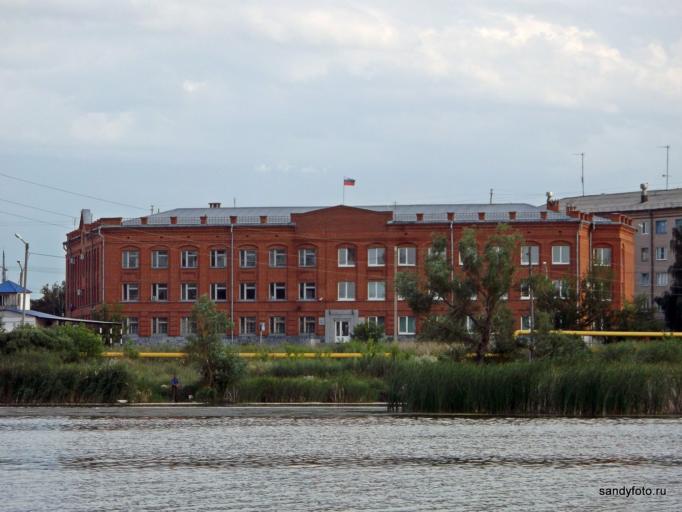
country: RU
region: Chelyabinsk
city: Troitsk
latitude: 54.0930
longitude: 61.5648
